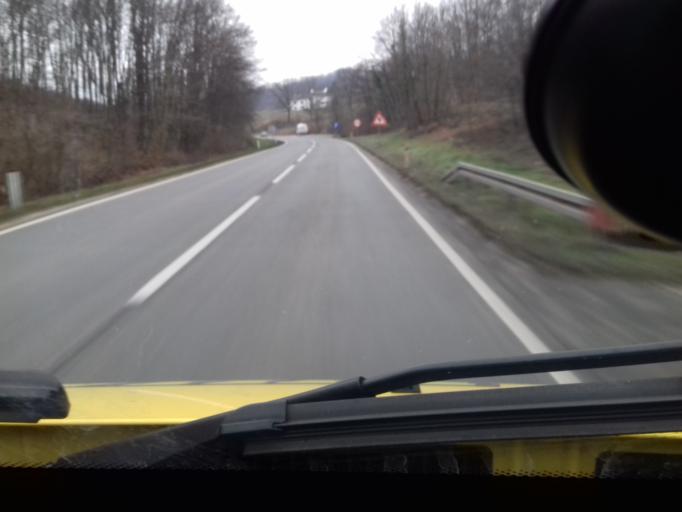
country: BA
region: Federation of Bosnia and Herzegovina
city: Lijesnica
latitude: 44.4689
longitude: 18.0671
